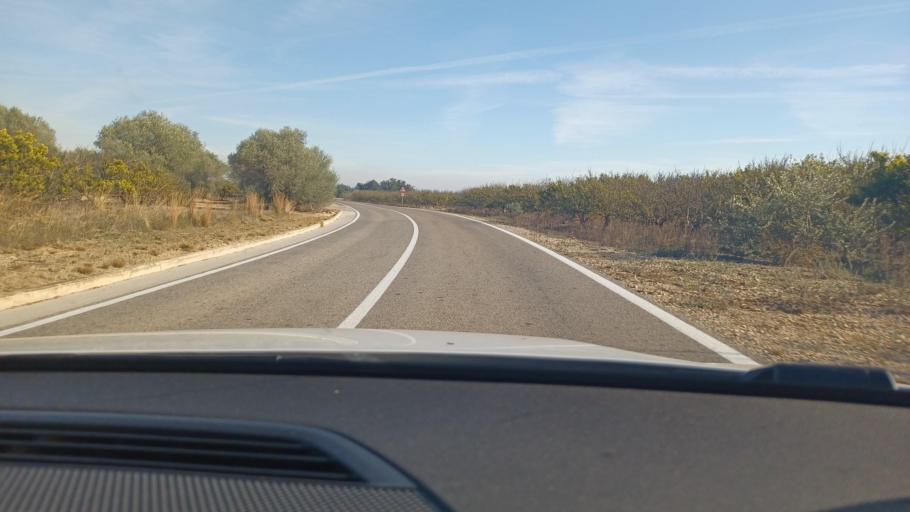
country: ES
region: Catalonia
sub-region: Provincia de Tarragona
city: Santa Barbara
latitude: 40.7216
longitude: 0.4423
